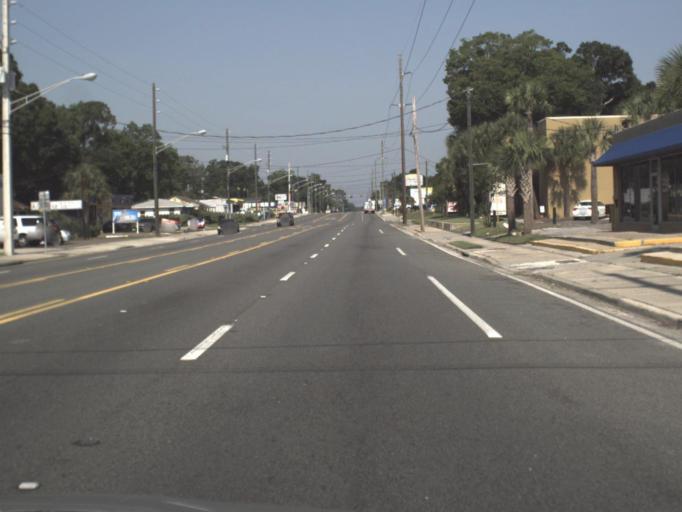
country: US
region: Florida
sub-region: Duval County
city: Jacksonville
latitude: 30.2822
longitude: -81.7268
